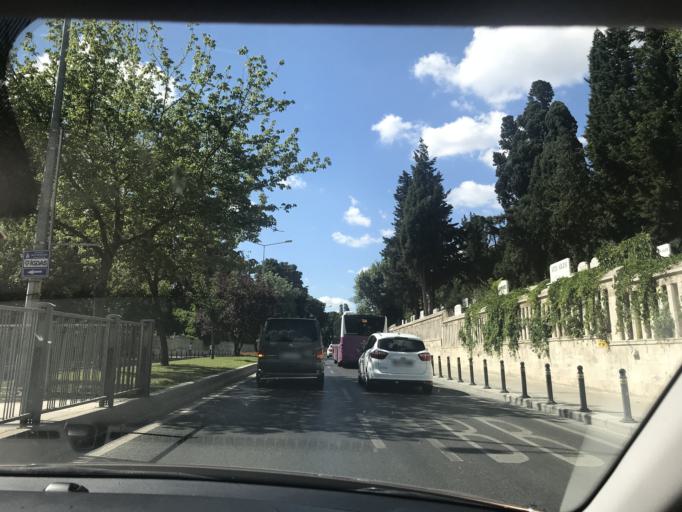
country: TR
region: Istanbul
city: UEskuedar
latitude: 41.0106
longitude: 29.0215
